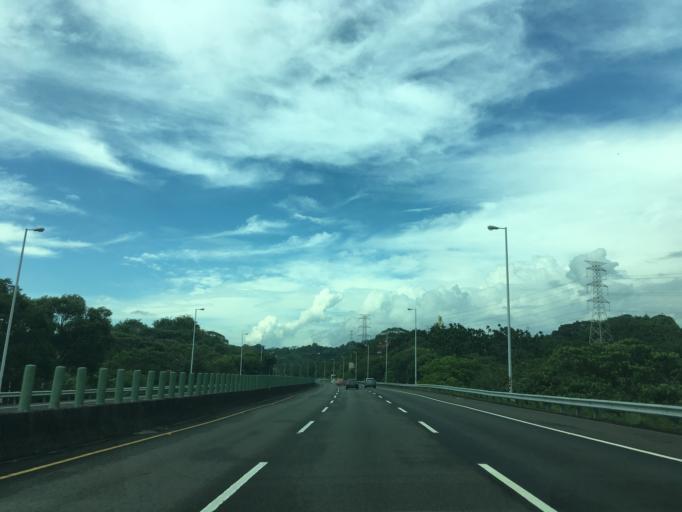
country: TW
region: Taiwan
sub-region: Chiayi
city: Jiayi Shi
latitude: 23.4630
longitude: 120.4961
